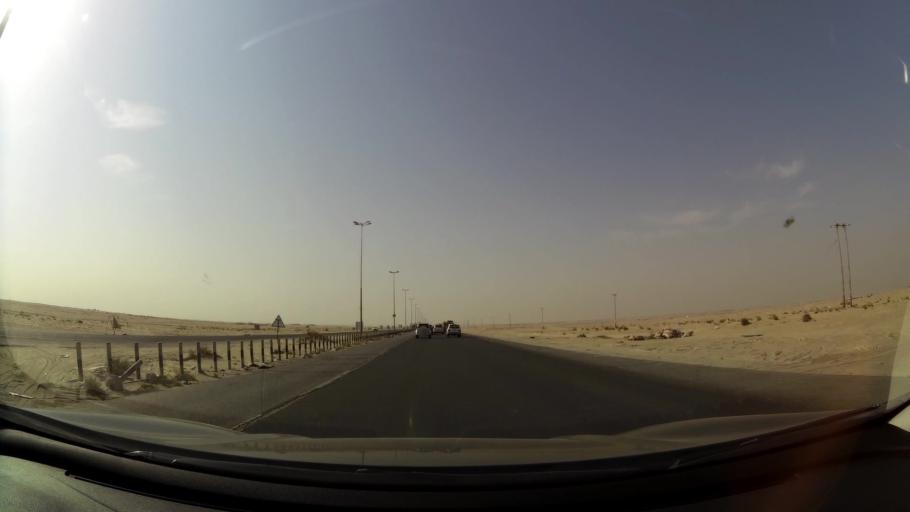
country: KW
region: Al Ahmadi
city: Al Ahmadi
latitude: 28.8814
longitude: 48.0805
